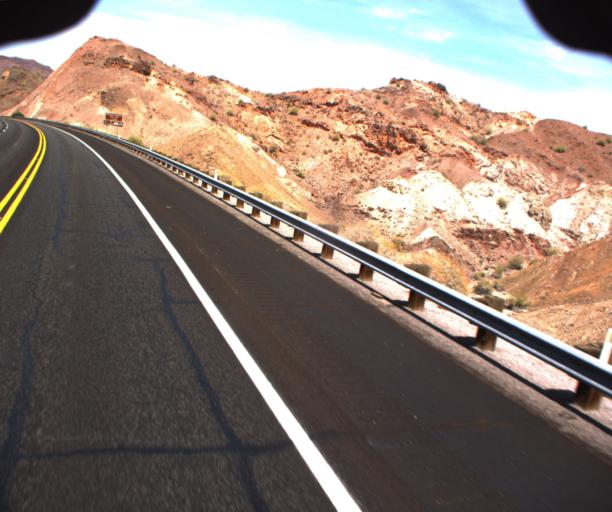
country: US
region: Arizona
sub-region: La Paz County
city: Cienega Springs
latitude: 34.2468
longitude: -114.1640
